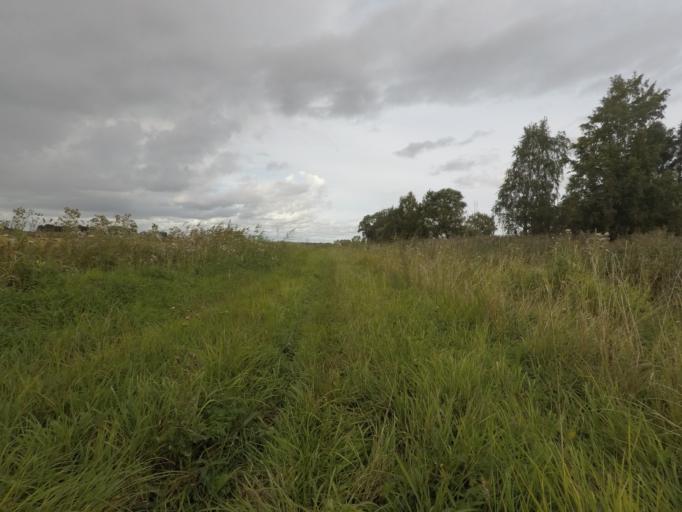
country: SE
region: Vaestmanland
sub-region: Kungsors Kommun
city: Kungsoer
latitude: 59.4620
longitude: 16.0602
